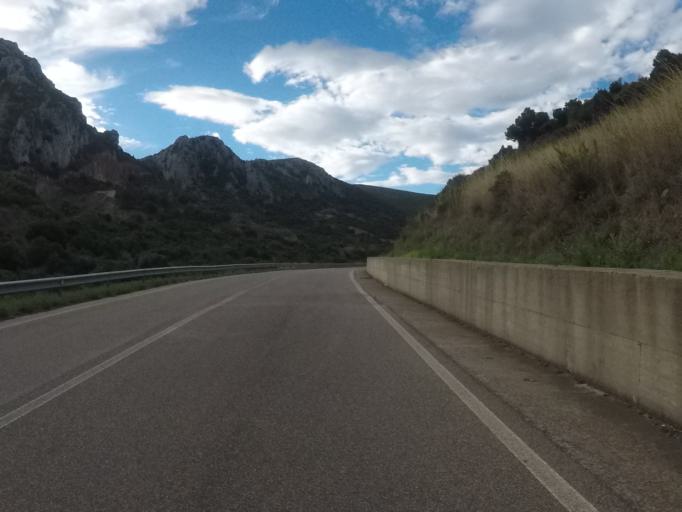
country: IT
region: Sardinia
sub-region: Provincia di Carbonia-Iglesias
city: Buggerru
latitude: 39.3612
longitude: 8.4403
